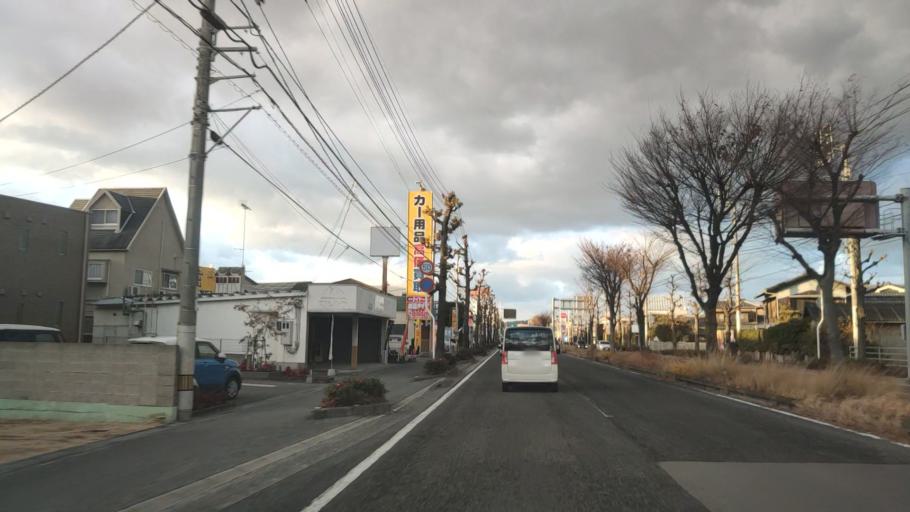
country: JP
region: Ehime
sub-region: Shikoku-chuo Shi
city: Matsuyama
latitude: 33.8050
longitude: 132.7820
